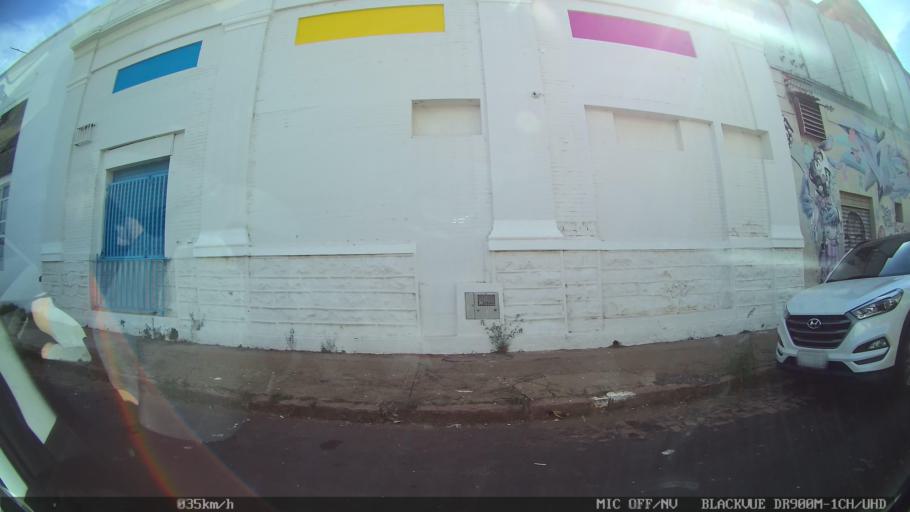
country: BR
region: Sao Paulo
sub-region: Franca
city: Franca
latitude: -20.5347
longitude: -47.4123
